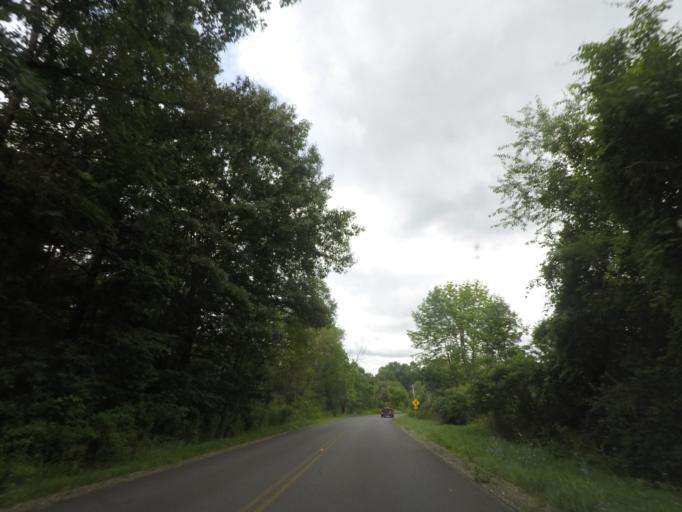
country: US
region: New York
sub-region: Saratoga County
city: Stillwater
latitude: 42.8692
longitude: -73.5579
